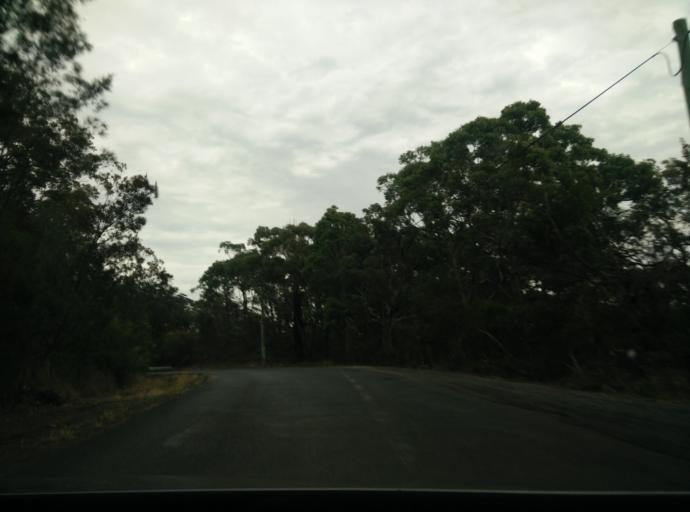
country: AU
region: New South Wales
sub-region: Gosford Shire
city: Narara
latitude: -33.3667
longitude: 151.3326
